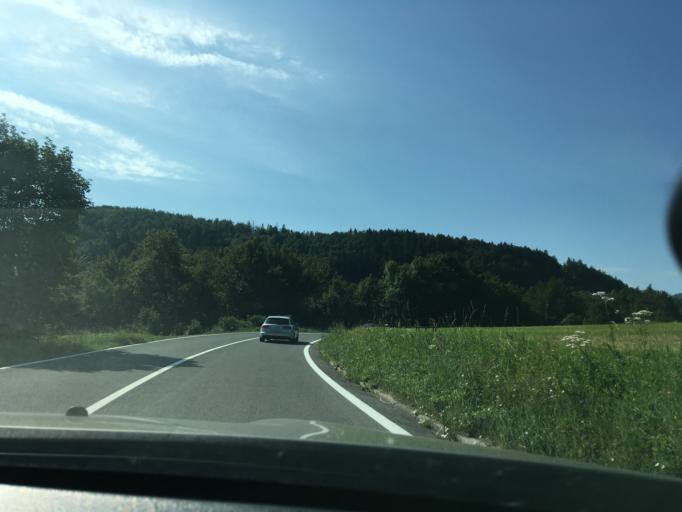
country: HR
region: Primorsko-Goranska
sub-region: Grad Delnice
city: Delnice
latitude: 45.4017
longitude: 14.8087
